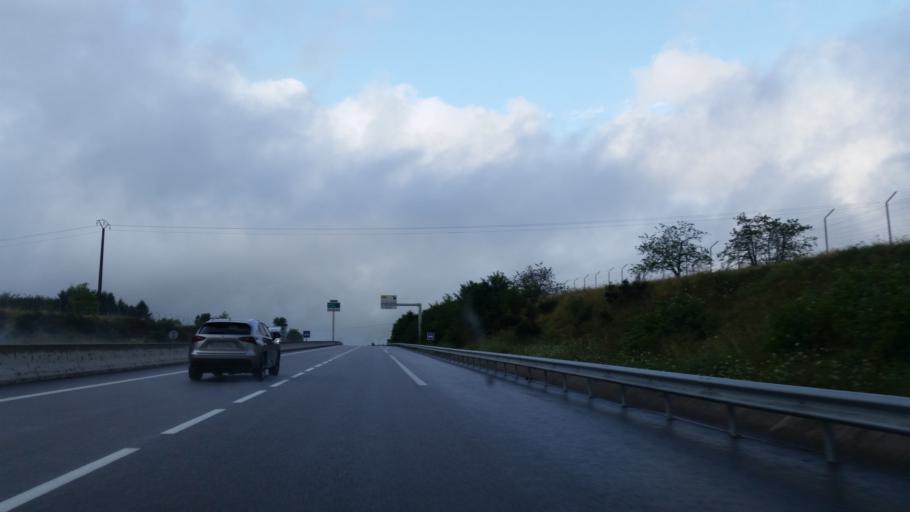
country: FR
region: Lorraine
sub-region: Departement des Vosges
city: Plombieres-les-Bains
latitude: 47.9414
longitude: 6.4533
